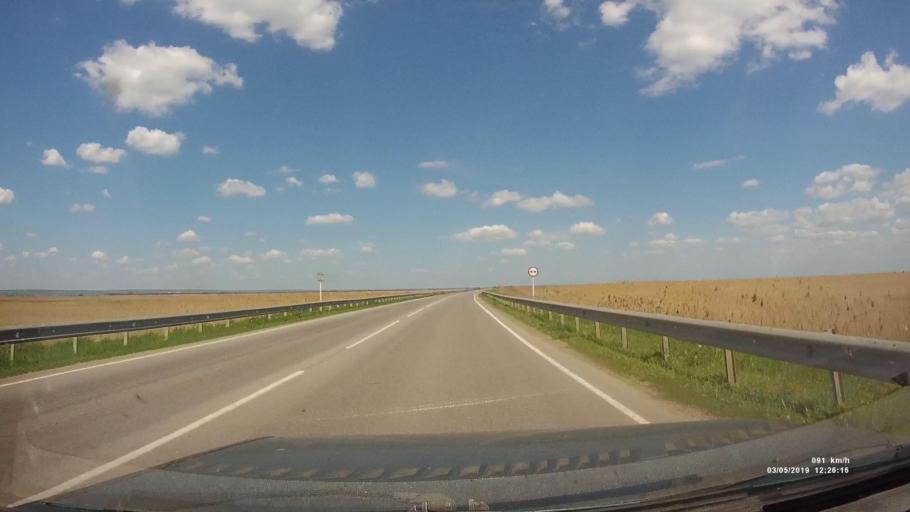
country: RU
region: Rostov
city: Semikarakorsk
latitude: 47.4428
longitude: 40.7126
